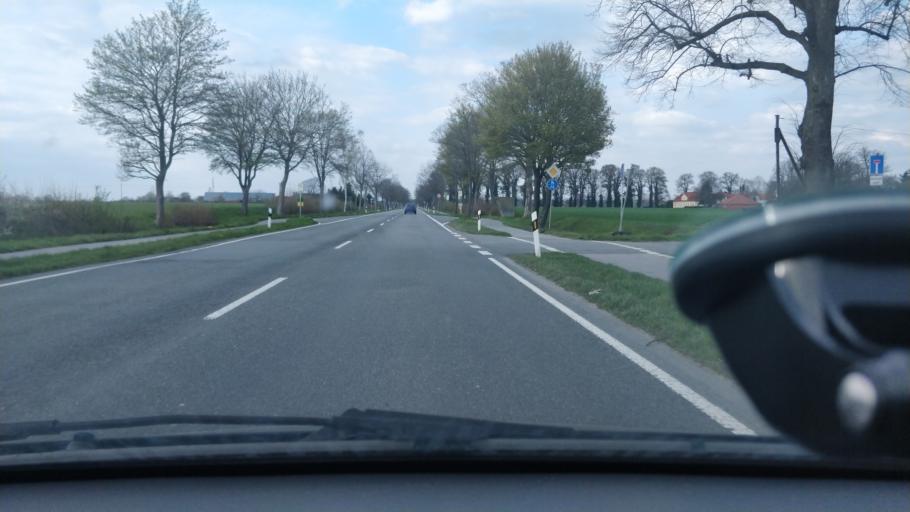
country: DE
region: North Rhine-Westphalia
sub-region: Regierungsbezirk Dusseldorf
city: Hamminkeln
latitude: 51.7082
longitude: 6.6000
